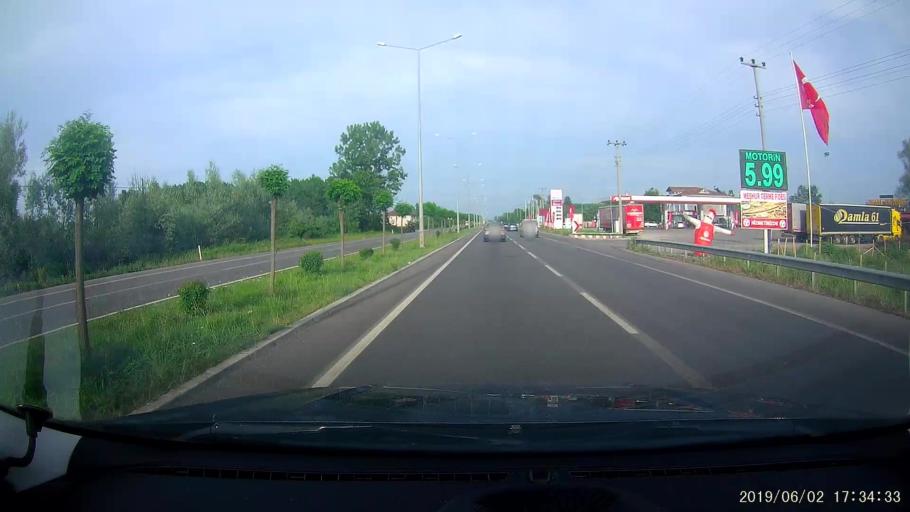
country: TR
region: Samsun
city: Terme
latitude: 41.2201
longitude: 36.8710
